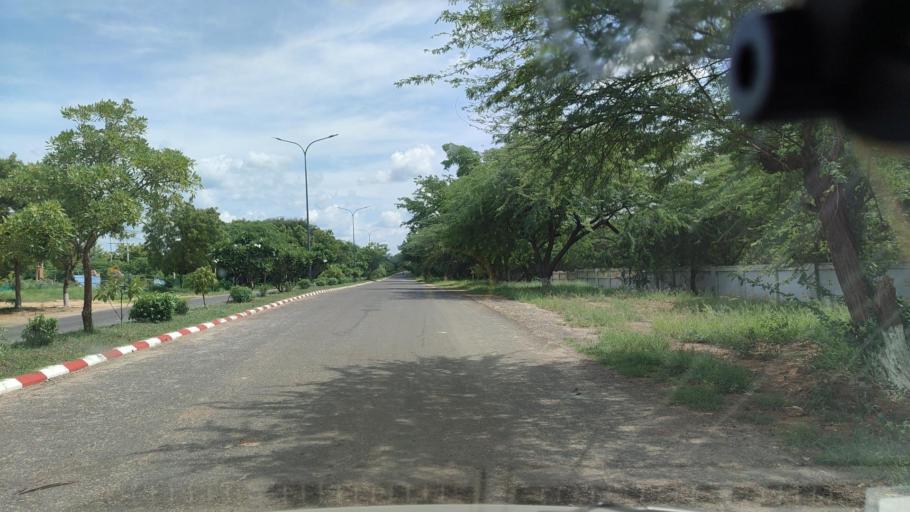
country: MM
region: Magway
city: Pakokku
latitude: 21.1657
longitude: 94.9240
